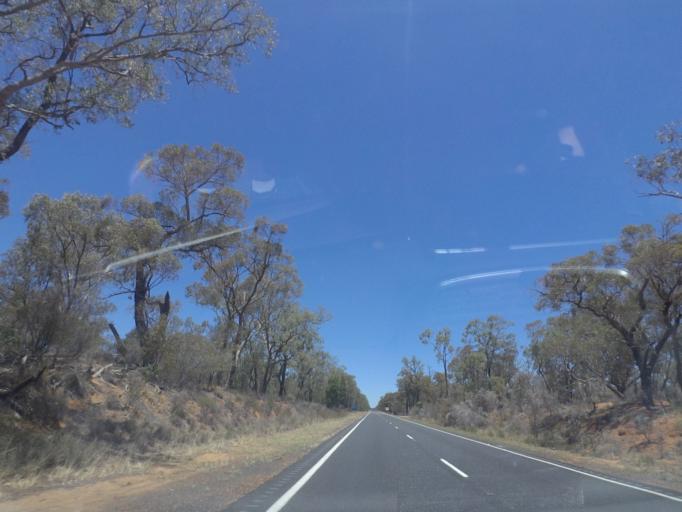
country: AU
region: New South Wales
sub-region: Warrumbungle Shire
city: Coonabarabran
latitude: -30.8563
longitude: 149.4560
